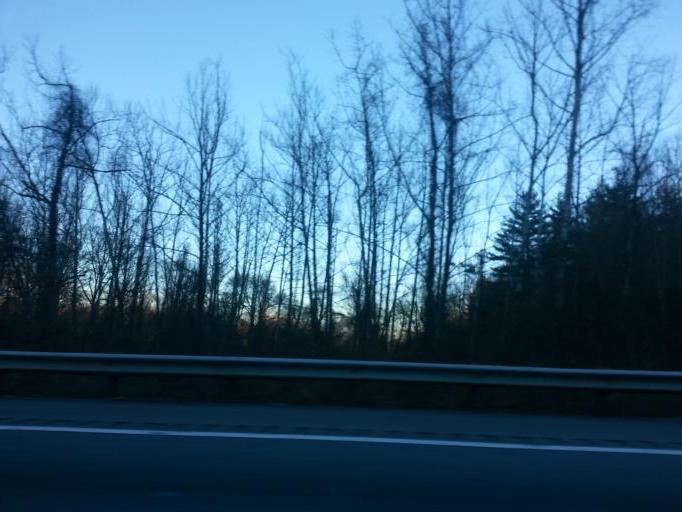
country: US
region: North Carolina
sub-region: Buncombe County
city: Bent Creek
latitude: 35.5077
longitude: -82.5721
